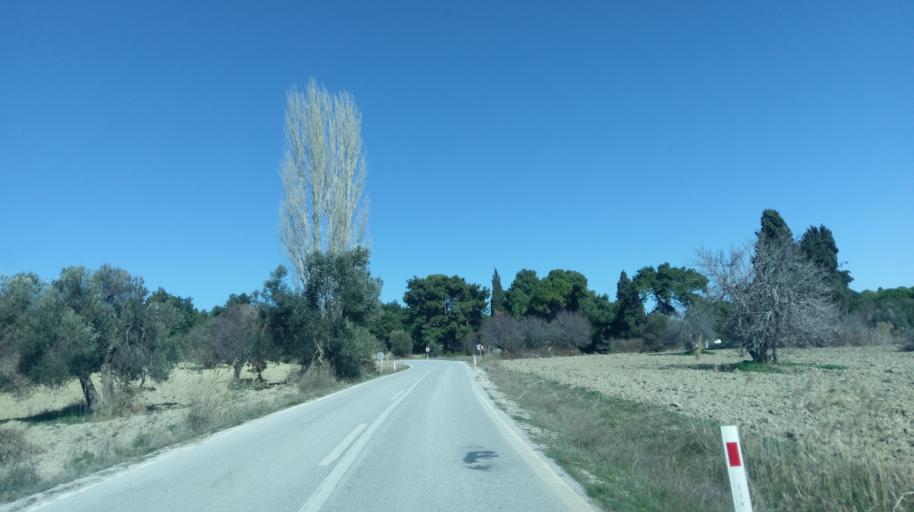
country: TR
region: Canakkale
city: Intepe
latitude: 40.0589
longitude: 26.1984
